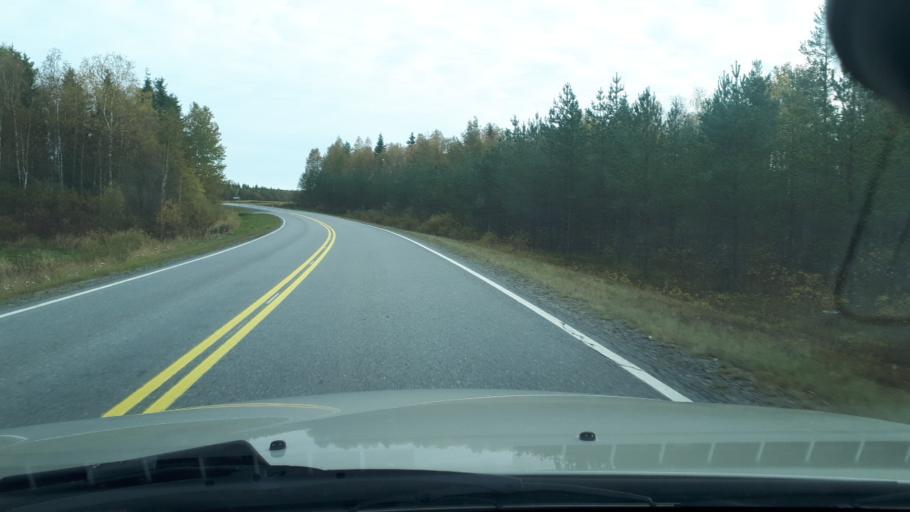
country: FI
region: Lapland
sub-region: Rovaniemi
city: Ranua
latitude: 66.0005
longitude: 26.2373
